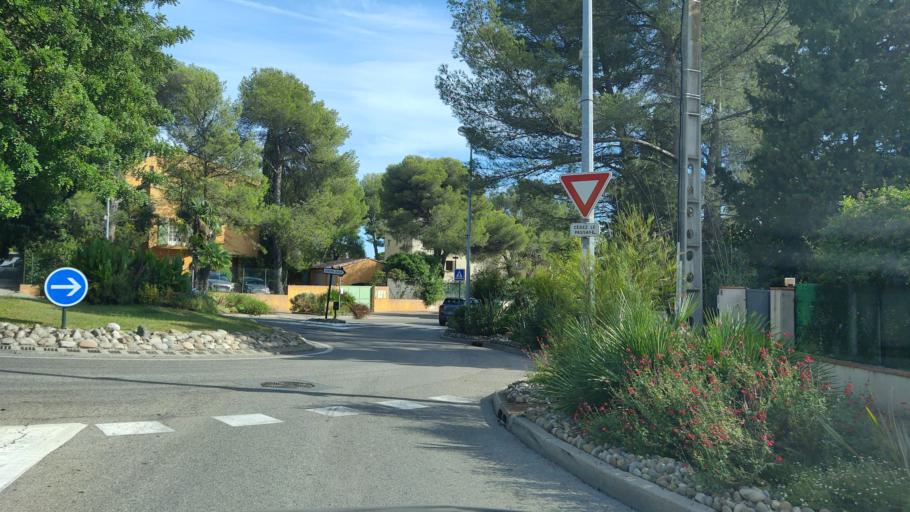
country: FR
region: Provence-Alpes-Cote d'Azur
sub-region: Departement du Var
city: Sanary-sur-Mer
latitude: 43.1241
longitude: 5.8028
